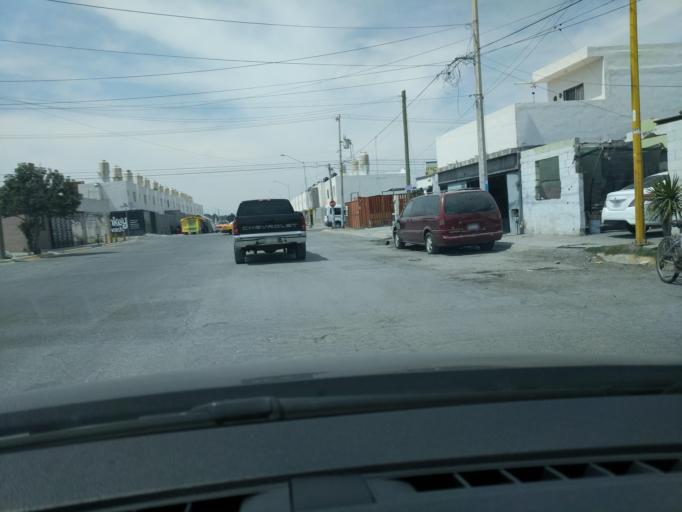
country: MX
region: Coahuila
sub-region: Arteaga
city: Arteaga
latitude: 25.4274
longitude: -100.9111
